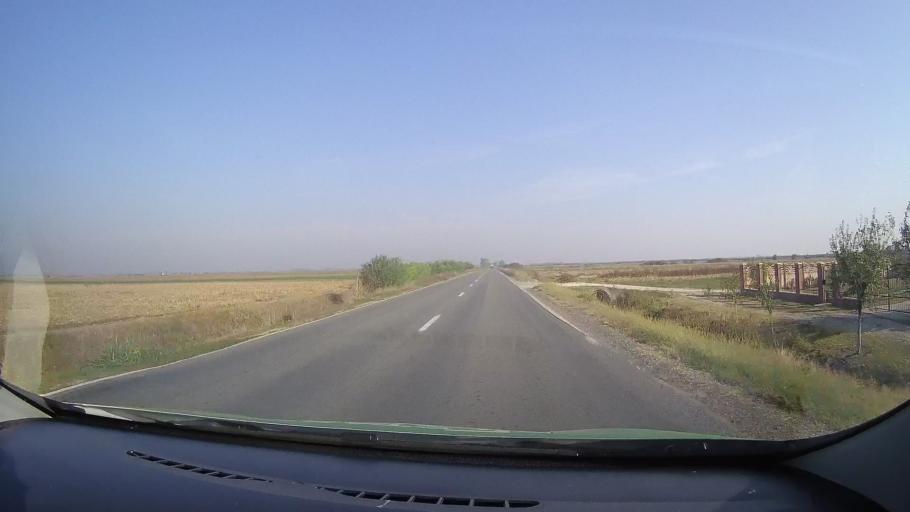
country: RO
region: Arad
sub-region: Comuna Pilu
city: Pilu
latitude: 46.5867
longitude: 21.3450
